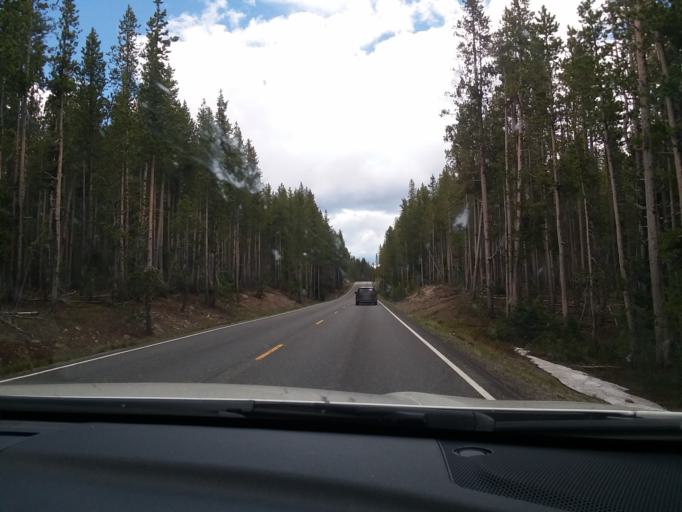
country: US
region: Idaho
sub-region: Teton County
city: Driggs
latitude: 44.1856
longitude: -110.6580
